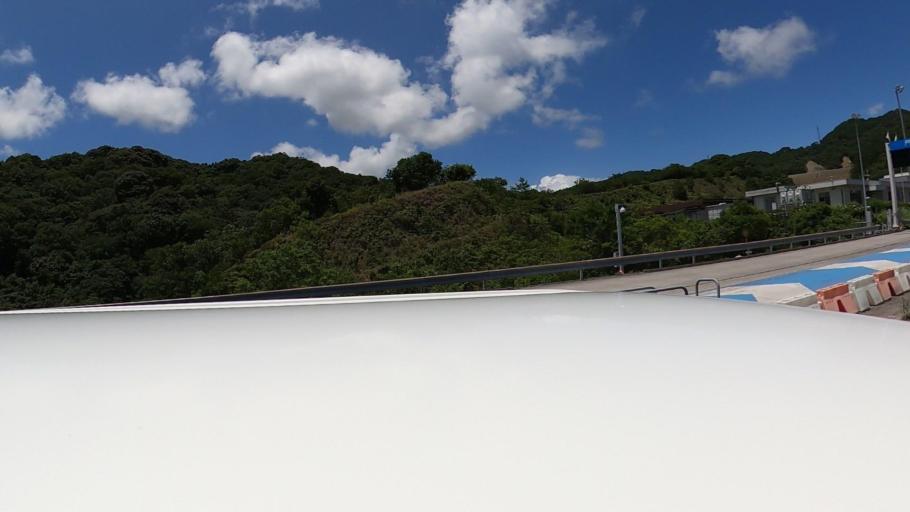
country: JP
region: Miyazaki
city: Nobeoka
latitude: 32.5024
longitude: 131.6619
